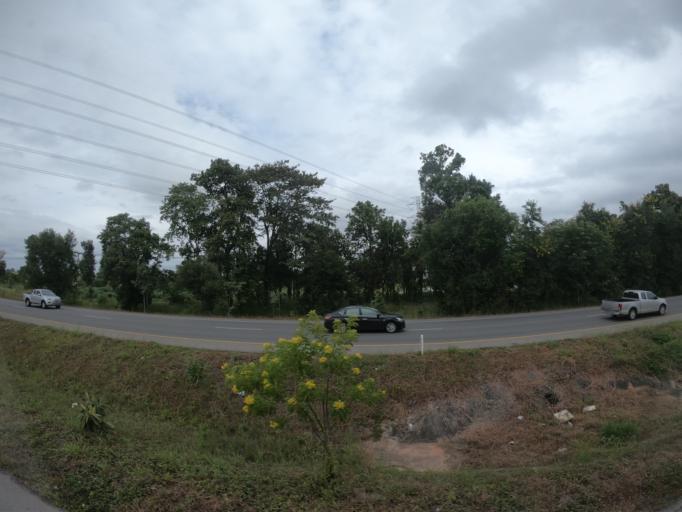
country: TH
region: Maha Sarakham
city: Kut Rang
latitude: 16.0452
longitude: 102.8759
